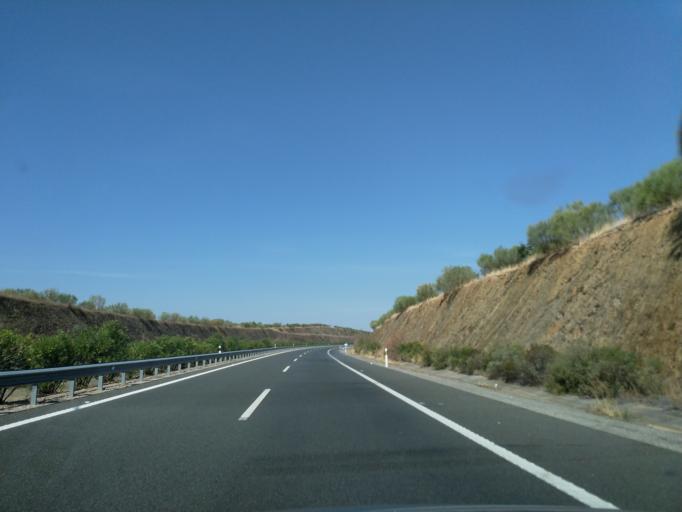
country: ES
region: Extremadura
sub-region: Provincia de Caceres
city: Aldea del Cano
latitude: 39.3384
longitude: -6.3377
